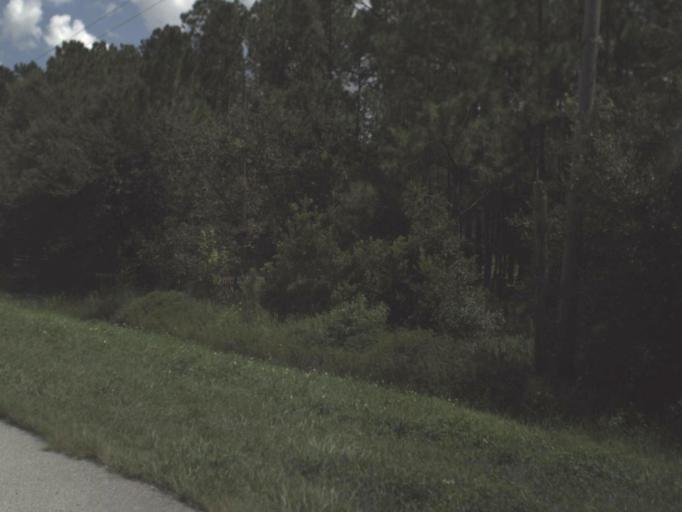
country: US
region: Florida
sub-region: Polk County
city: Babson Park
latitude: 27.8051
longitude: -81.2329
